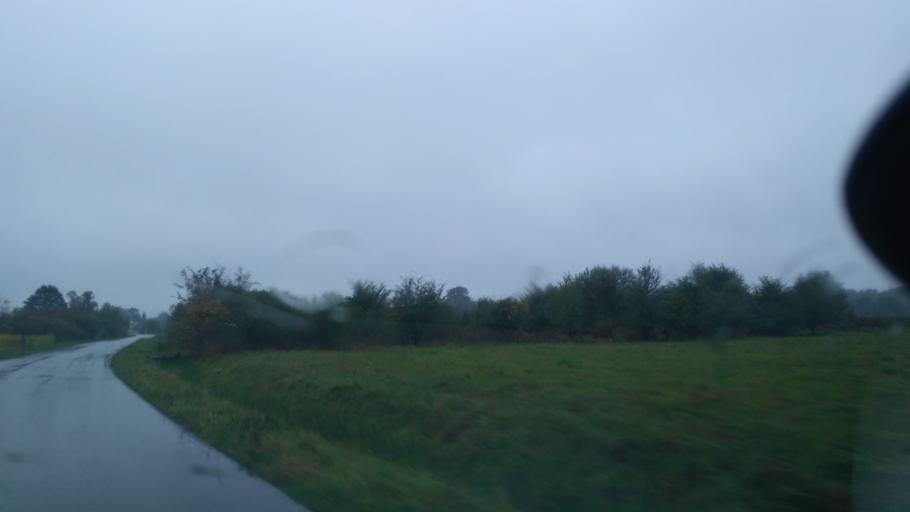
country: PL
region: Subcarpathian Voivodeship
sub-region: Powiat krosnienski
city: Kroscienko Wyzne
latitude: 49.6647
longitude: 21.8040
